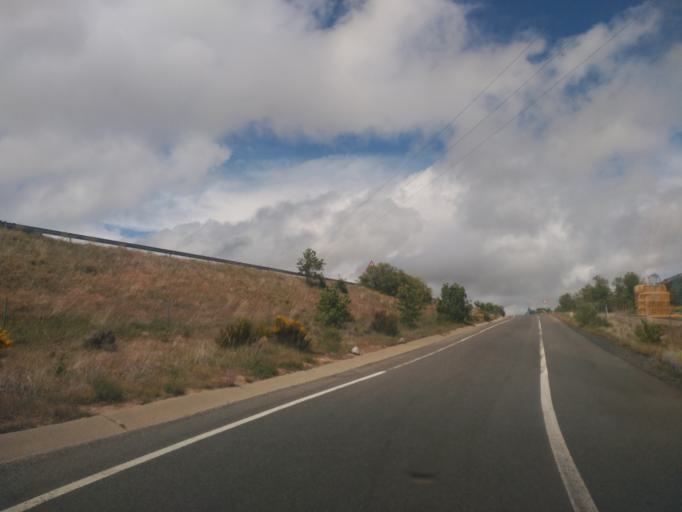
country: ES
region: Castille and Leon
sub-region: Provincia de Salamanca
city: Vallejera de Riofrio
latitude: 40.4109
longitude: -5.7201
